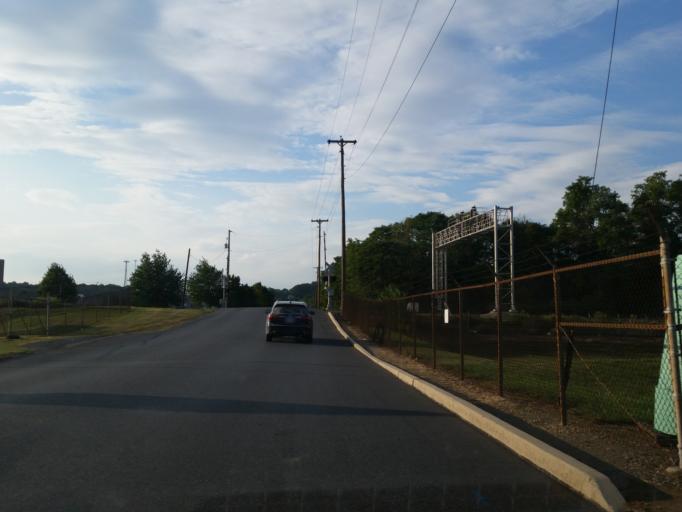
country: US
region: Pennsylvania
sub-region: Lebanon County
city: Palmyra
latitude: 40.3151
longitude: -76.5889
